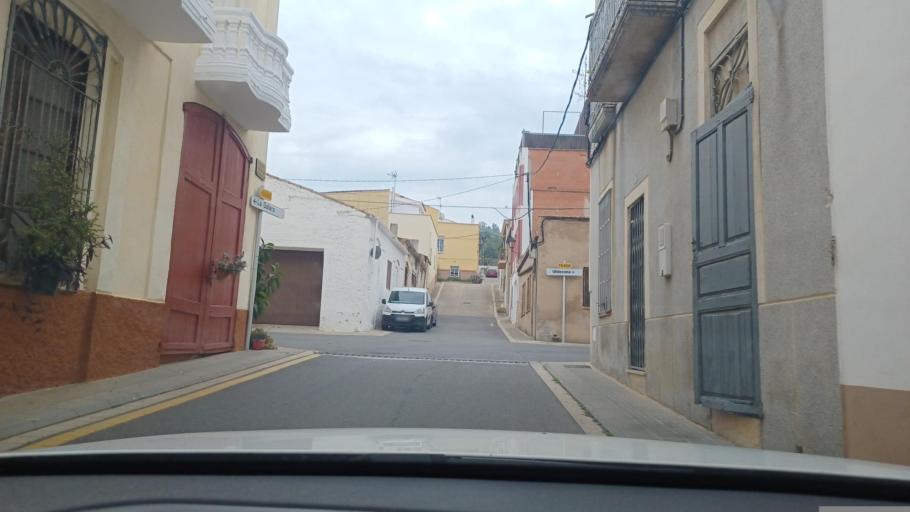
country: ES
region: Catalonia
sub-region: Provincia de Tarragona
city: Ulldecona
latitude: 40.6543
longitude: 0.4697
